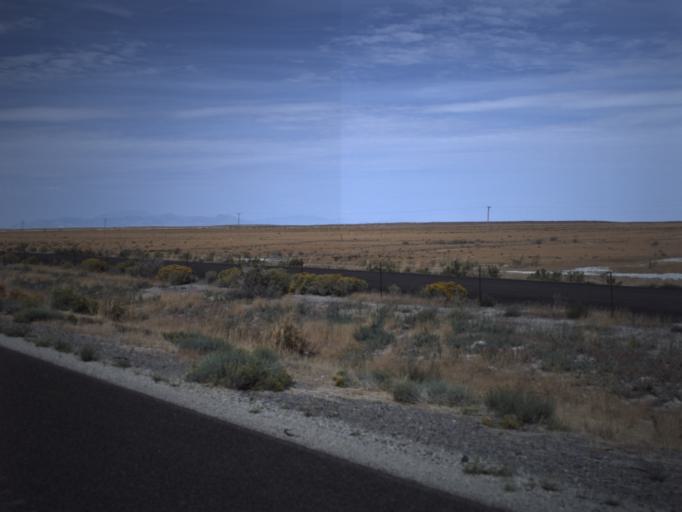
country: US
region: Utah
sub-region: Tooele County
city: Grantsville
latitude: 40.7268
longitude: -113.2112
